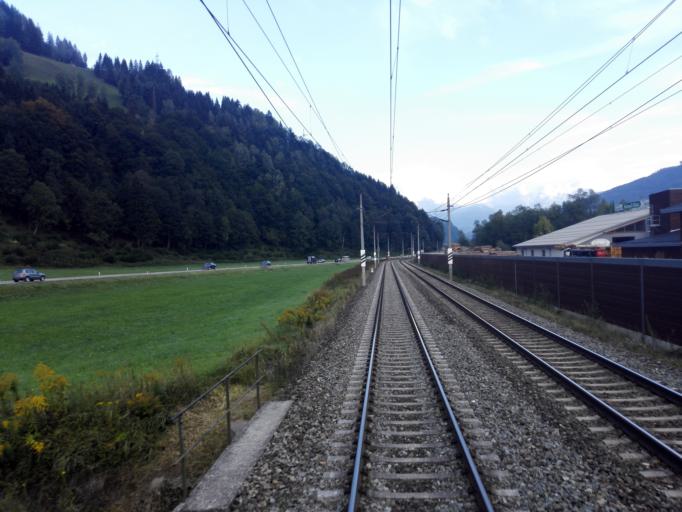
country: AT
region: Salzburg
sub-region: Politischer Bezirk Sankt Johann im Pongau
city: Sankt Johann im Pongau
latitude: 47.3728
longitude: 13.2077
